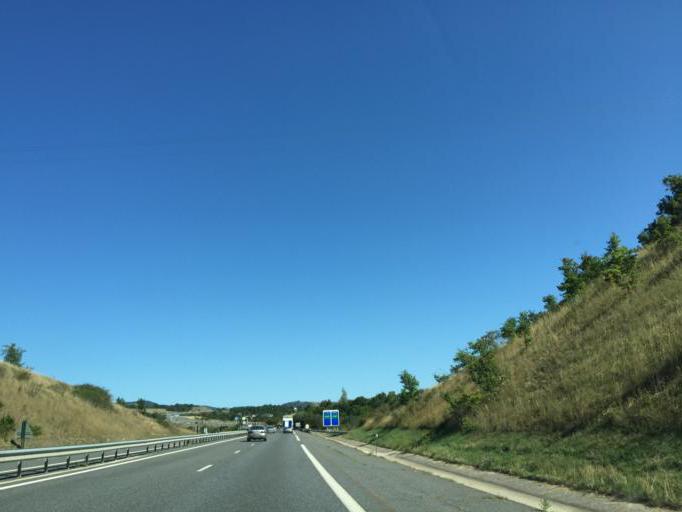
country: FR
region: Midi-Pyrenees
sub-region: Departement de l'Aveyron
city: Severac-le-Chateau
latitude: 44.3347
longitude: 3.0573
